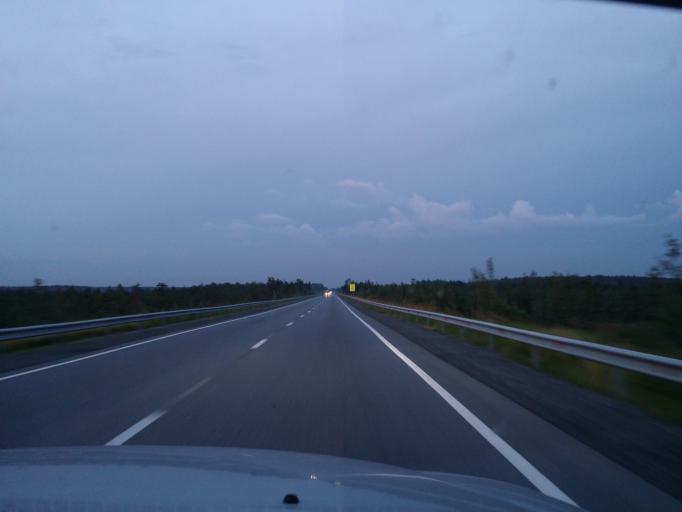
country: RU
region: Khanty-Mansiyskiy Avtonomnyy Okrug
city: Poykovskiy
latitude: 61.3573
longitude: 73.3427
